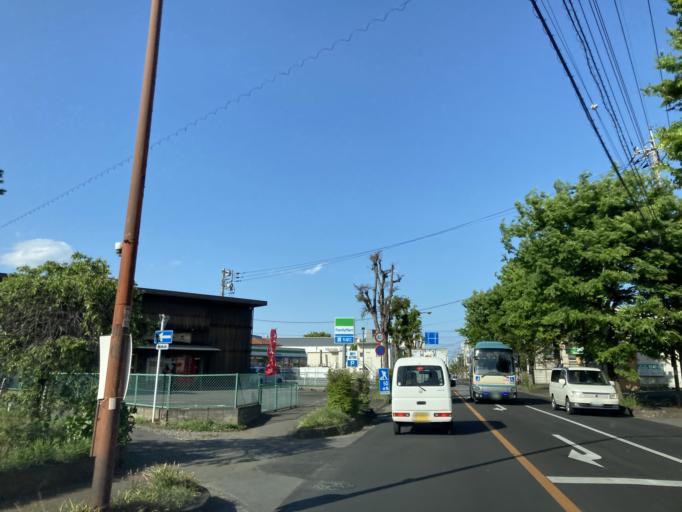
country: JP
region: Saitama
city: Sayama
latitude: 35.8722
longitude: 139.4378
